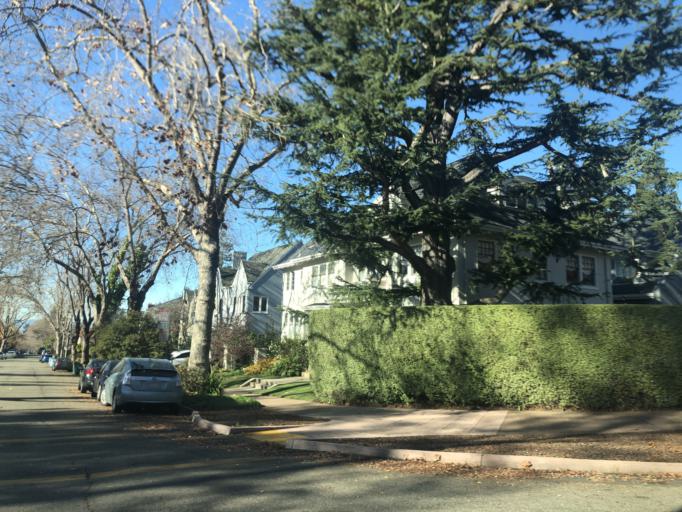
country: US
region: California
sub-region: Alameda County
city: Berkeley
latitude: 37.8618
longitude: -122.2470
